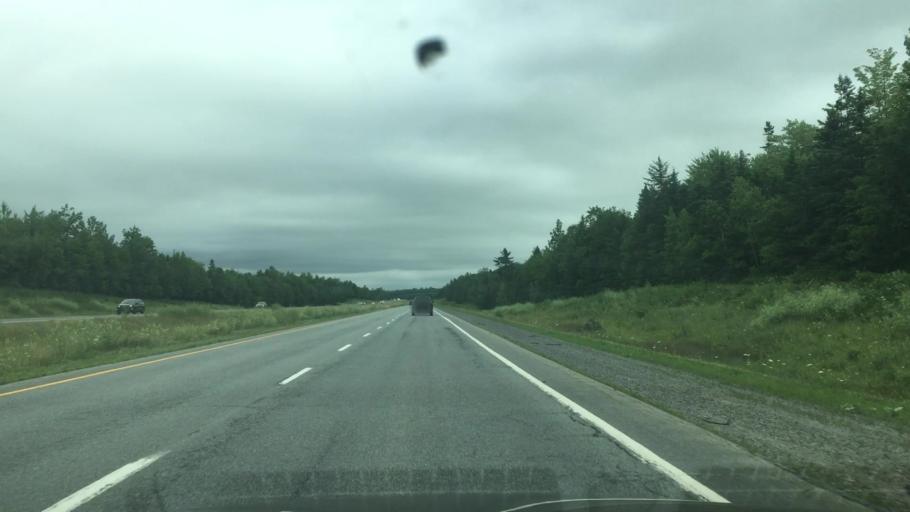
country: CA
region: Nova Scotia
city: Cole Harbour
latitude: 45.0083
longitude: -63.4803
